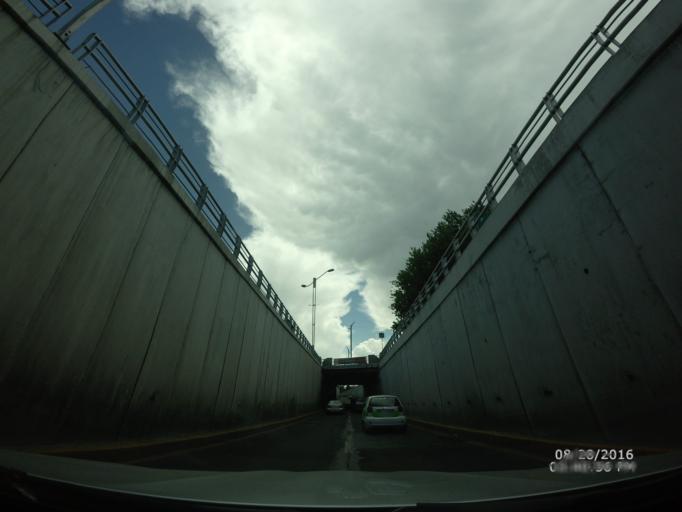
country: MX
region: Hidalgo
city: Pachuca de Soto
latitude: 20.1114
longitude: -98.7468
